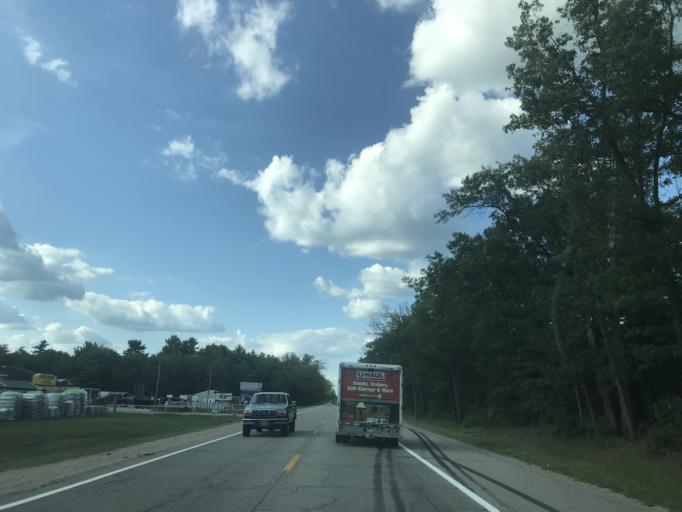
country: US
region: Michigan
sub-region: Newaygo County
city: White Cloud
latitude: 43.4873
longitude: -85.7733
